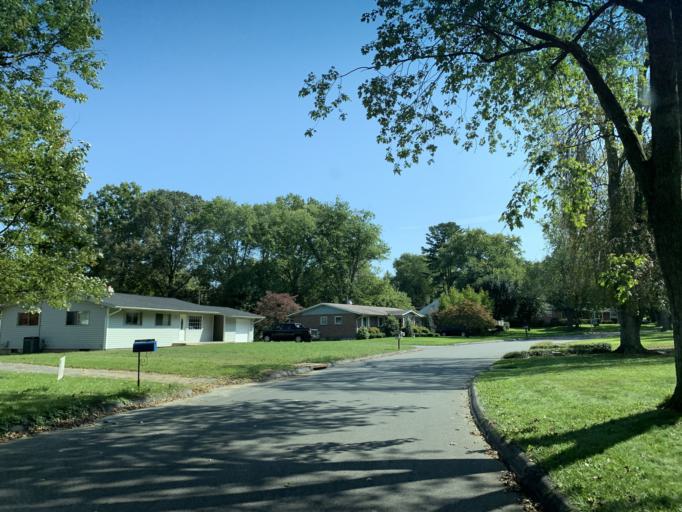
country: US
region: Maryland
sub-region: Harford County
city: South Bel Air
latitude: 39.5213
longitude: -76.3385
